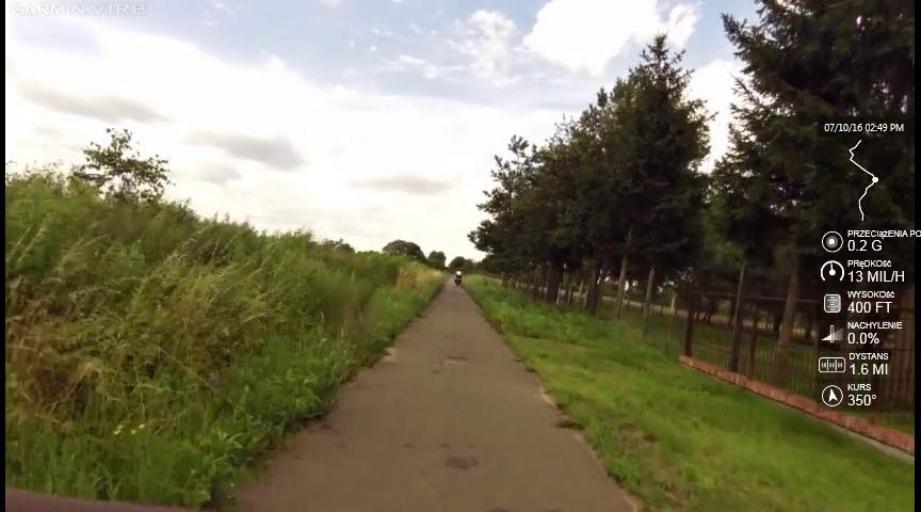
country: PL
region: West Pomeranian Voivodeship
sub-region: Powiat gryfinski
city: Banie
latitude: 53.0972
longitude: 14.6501
